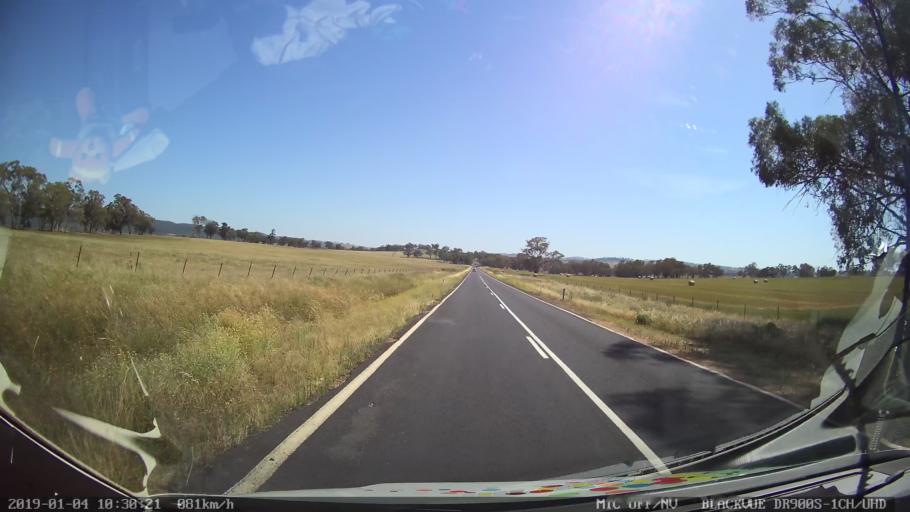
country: AU
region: New South Wales
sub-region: Cabonne
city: Canowindra
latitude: -33.3468
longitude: 148.6273
